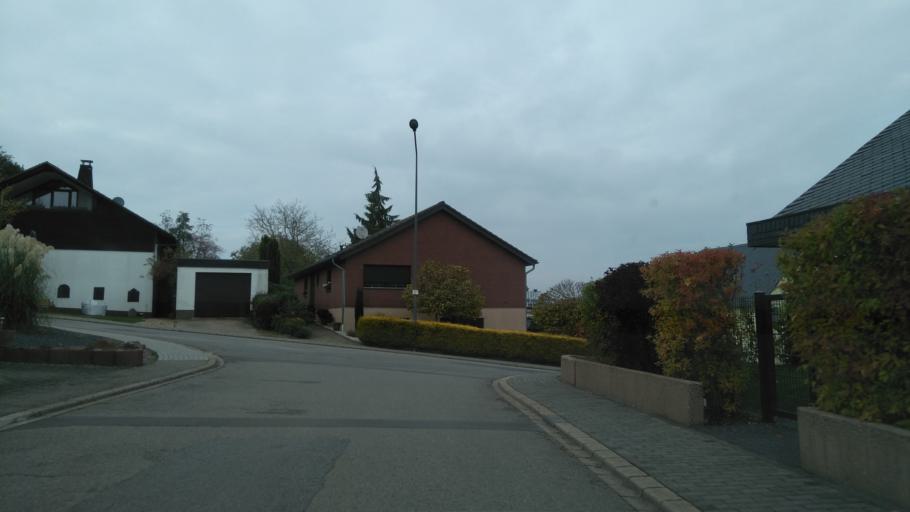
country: DE
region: Rheinland-Pfalz
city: Pellingen
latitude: 49.6754
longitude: 6.6679
